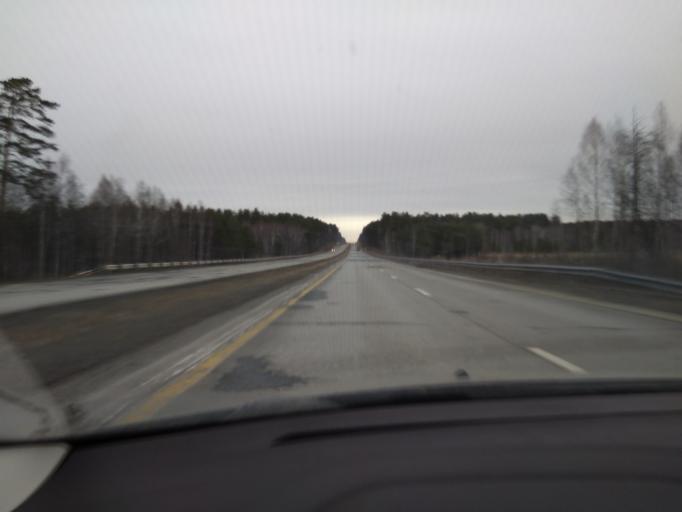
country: RU
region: Sverdlovsk
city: Sysert'
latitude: 56.4239
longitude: 60.8744
